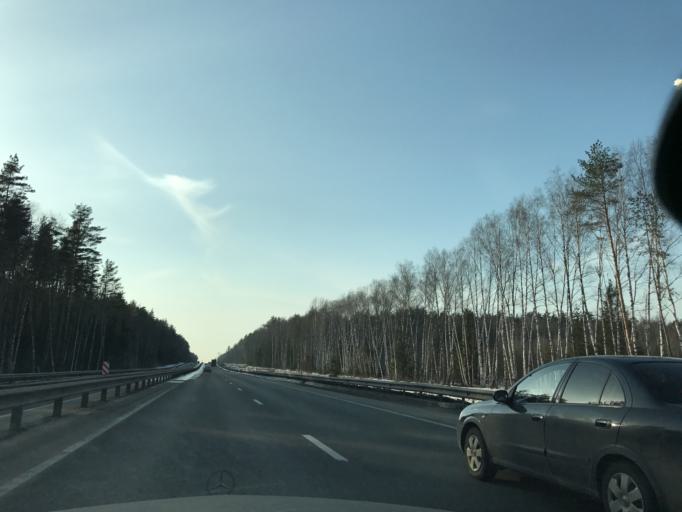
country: RU
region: Vladimir
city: Nikologory
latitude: 56.2360
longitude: 41.9183
